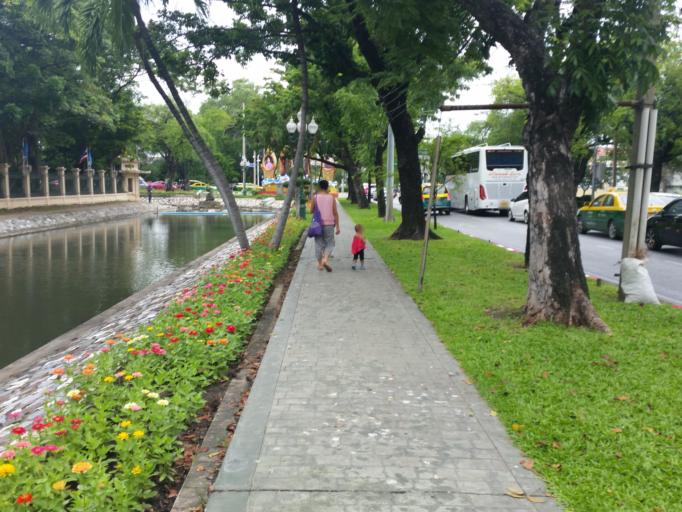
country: TH
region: Bangkok
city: Pom Prap Sattru Phai
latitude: 13.7673
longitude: 100.5158
